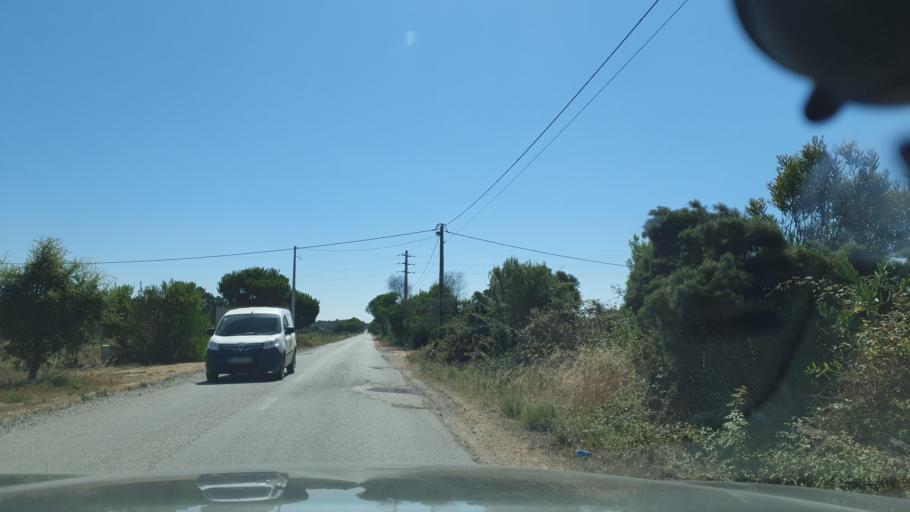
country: PT
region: Beja
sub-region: Odemira
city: Sao Teotonio
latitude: 37.5013
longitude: -8.6852
